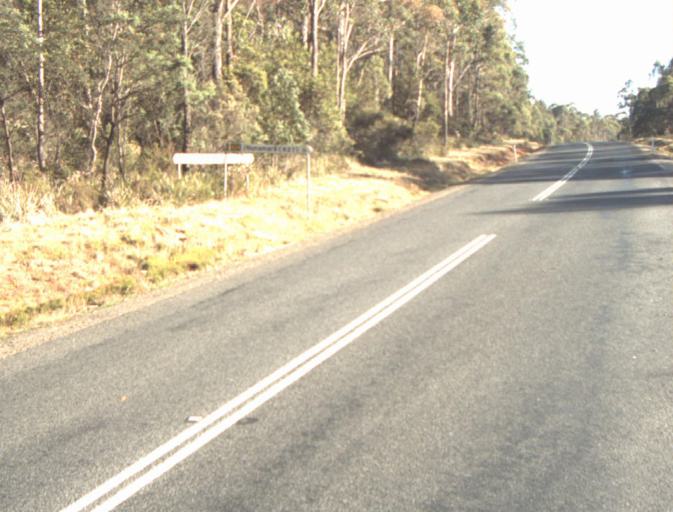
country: AU
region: Tasmania
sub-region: Launceston
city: Mayfield
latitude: -41.3343
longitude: 147.1787
